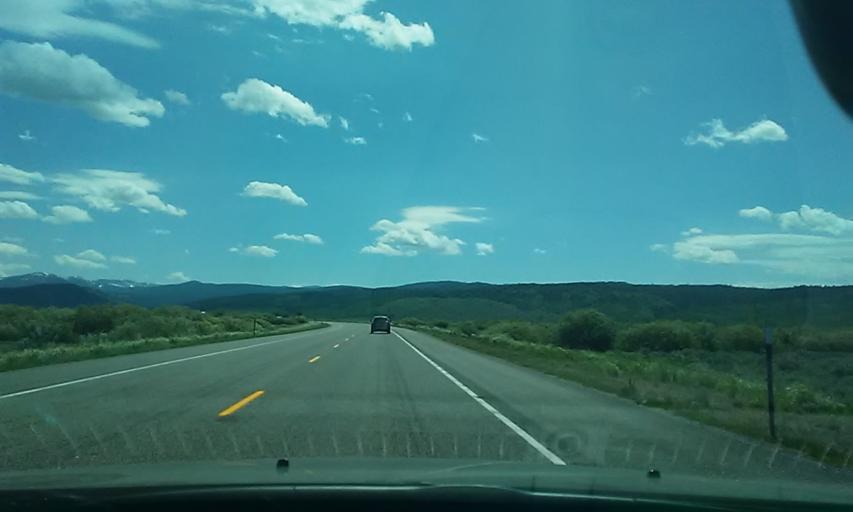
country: US
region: Wyoming
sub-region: Teton County
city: Jackson
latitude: 43.8337
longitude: -110.4266
